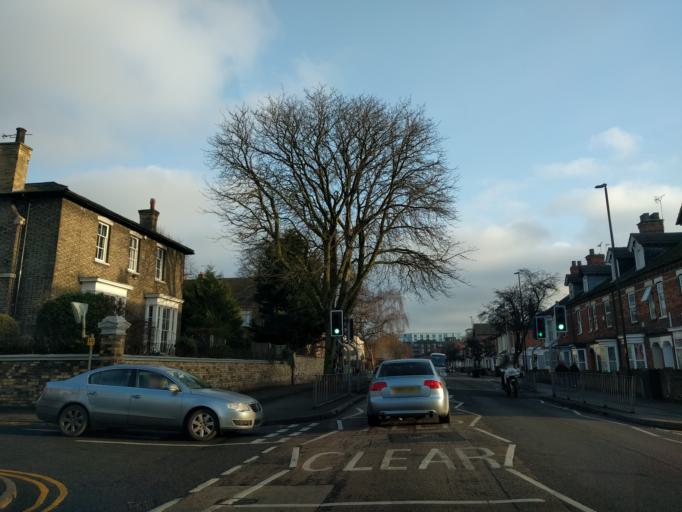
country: GB
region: England
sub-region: Lincolnshire
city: Lincoln
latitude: 53.2321
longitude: -0.5530
